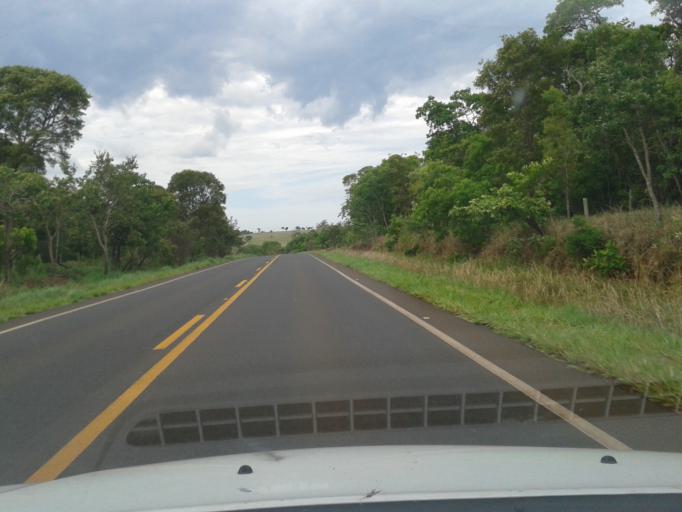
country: BR
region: Minas Gerais
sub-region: Iturama
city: Iturama
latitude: -19.6062
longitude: -50.0507
